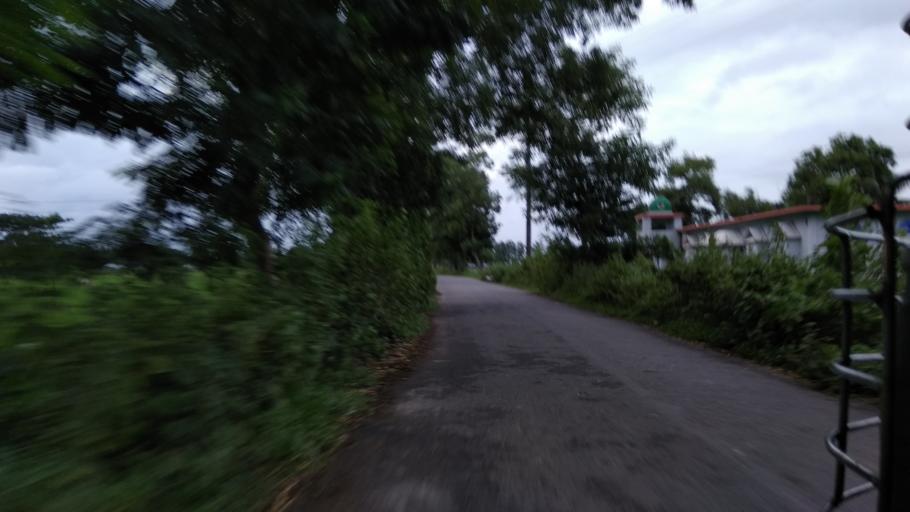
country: IN
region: Tripura
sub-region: Dhalai
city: Kamalpur
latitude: 24.2218
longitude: 91.8549
